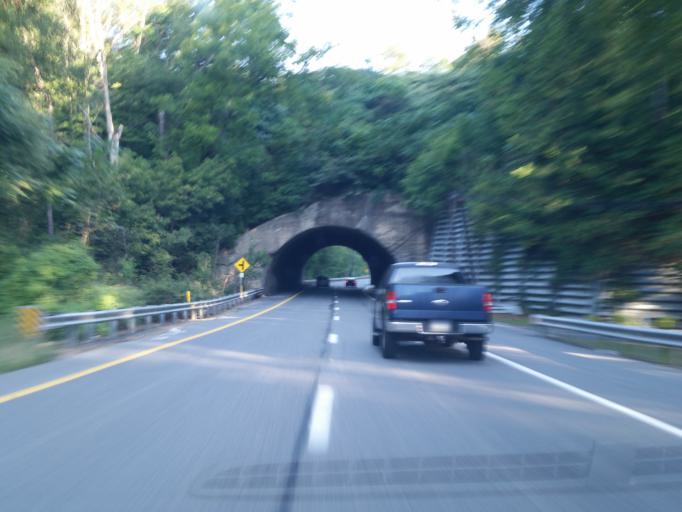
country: US
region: Pennsylvania
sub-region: Lancaster County
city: Willow Street
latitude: 39.9250
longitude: -76.2508
